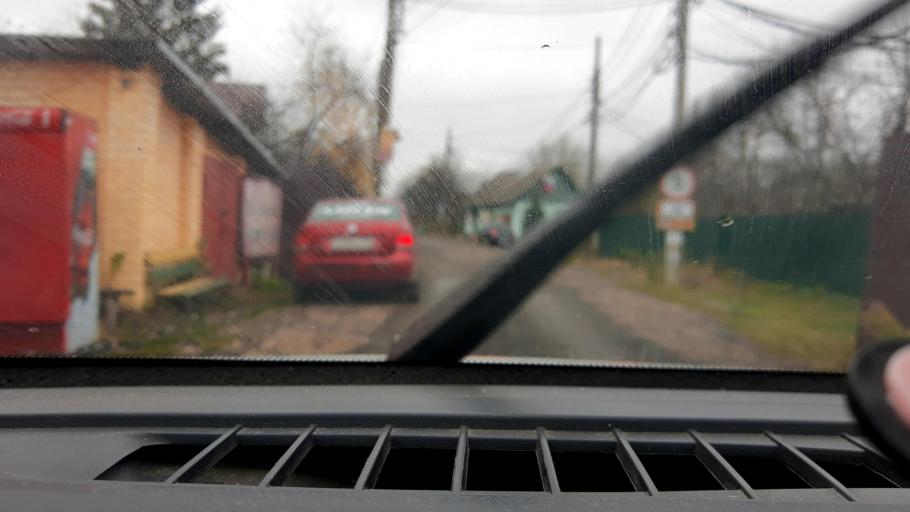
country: RU
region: Nizjnij Novgorod
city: Gorbatovka
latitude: 56.3823
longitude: 43.8120
